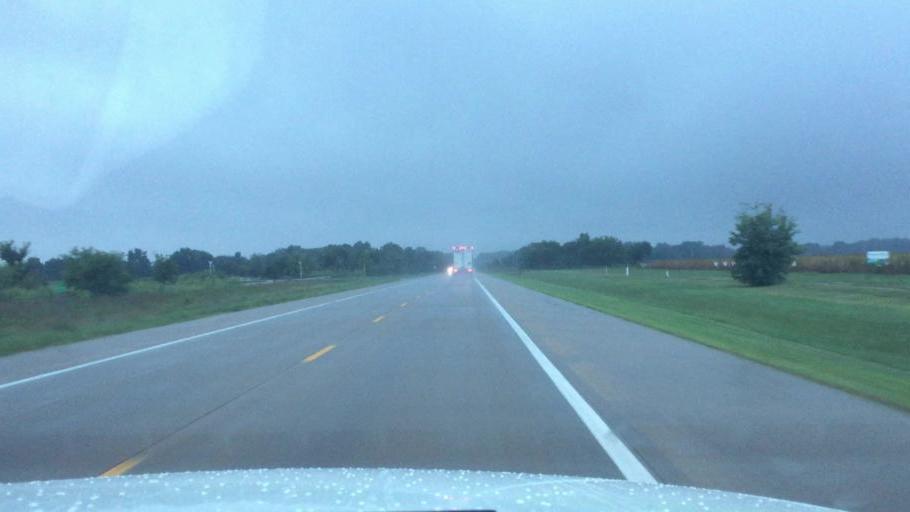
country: US
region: Kansas
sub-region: Neosho County
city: Chanute
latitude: 37.5634
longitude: -95.4710
